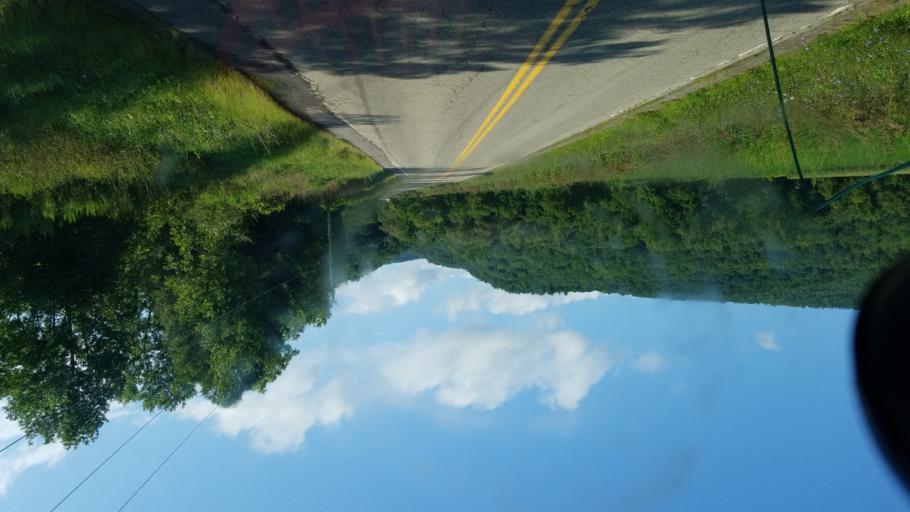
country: US
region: New York
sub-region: Steuben County
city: Canisteo
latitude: 42.2618
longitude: -77.5816
